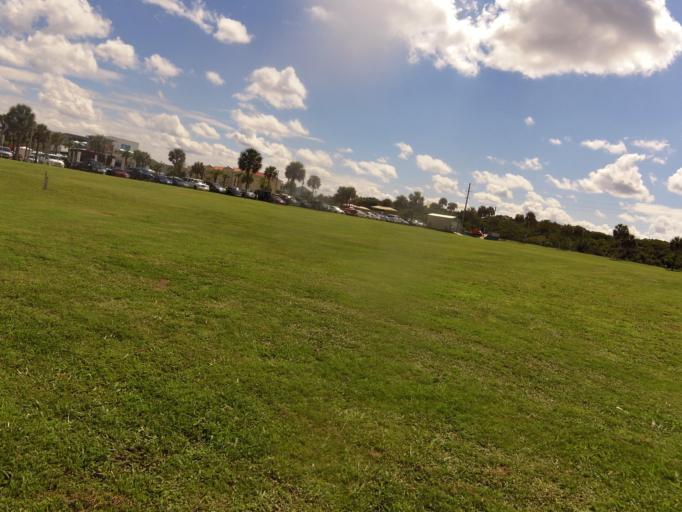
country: US
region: Florida
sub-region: Nassau County
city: Fernandina Beach
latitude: 30.6698
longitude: -81.4313
